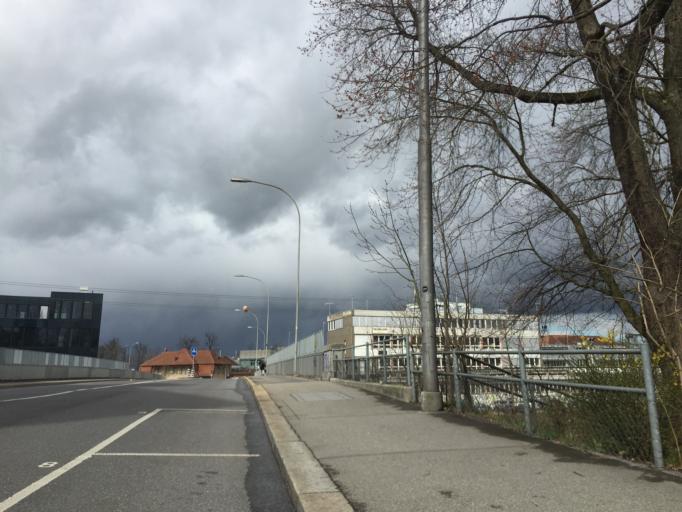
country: CH
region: Bern
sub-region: Bern-Mittelland District
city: Bern
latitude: 46.9646
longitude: 7.4548
